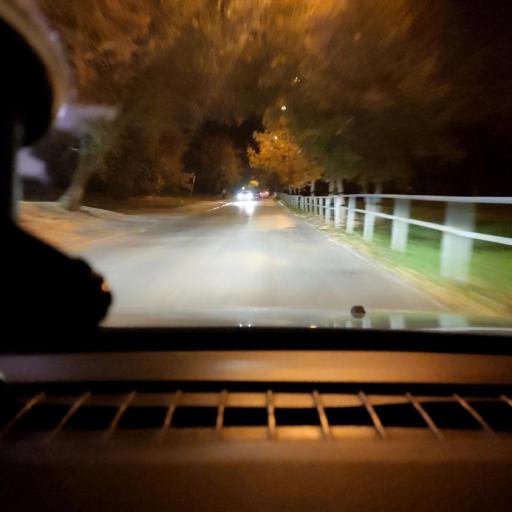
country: RU
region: Samara
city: Samara
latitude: 53.2412
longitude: 50.2228
